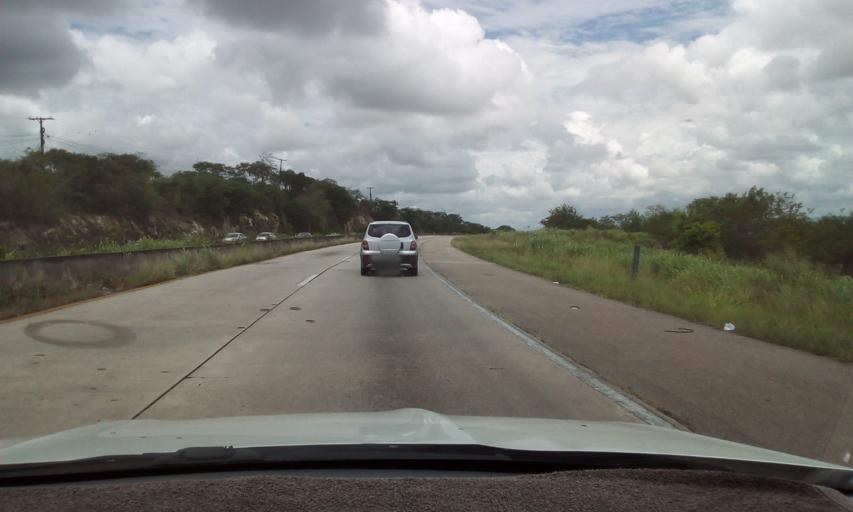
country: BR
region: Pernambuco
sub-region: Gravata
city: Gravata
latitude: -8.1972
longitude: -35.5214
